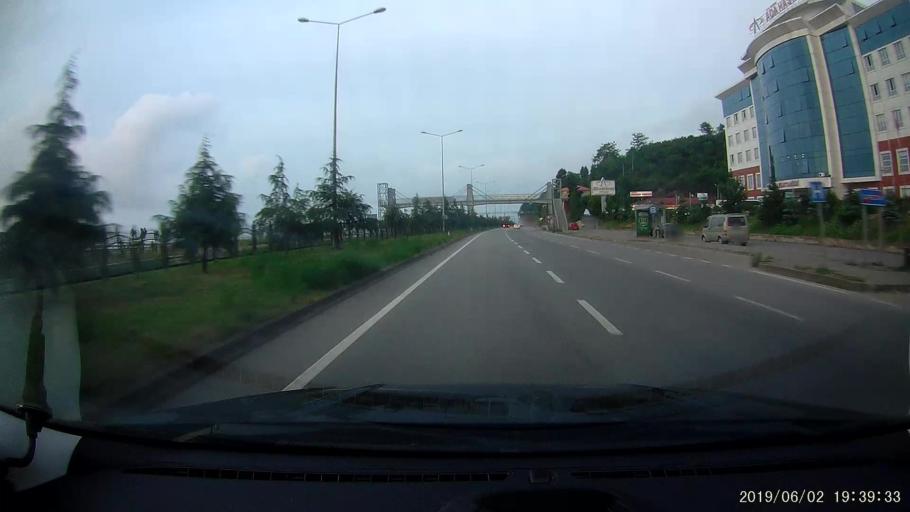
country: TR
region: Giresun
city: Giresun
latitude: 40.9135
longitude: 38.4432
